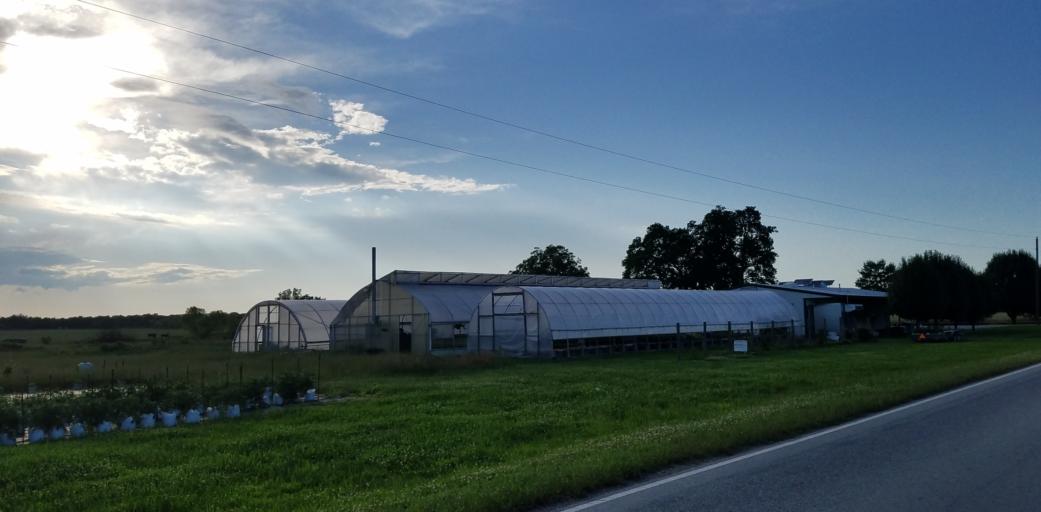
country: US
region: Oklahoma
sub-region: Coal County
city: Coalgate
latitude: 34.4767
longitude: -96.4241
